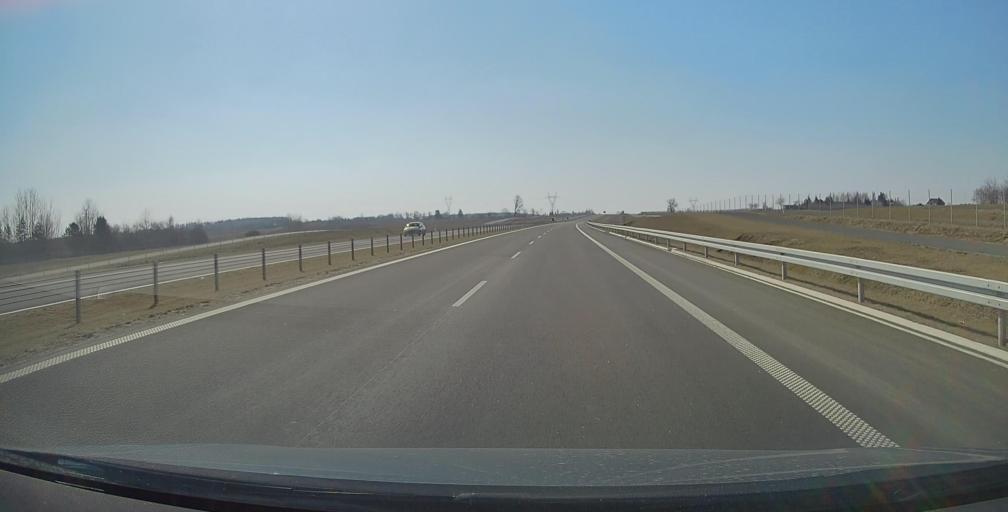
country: PL
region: Lublin Voivodeship
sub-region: Powiat krasnicki
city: Szastarka
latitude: 50.8089
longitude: 22.2992
